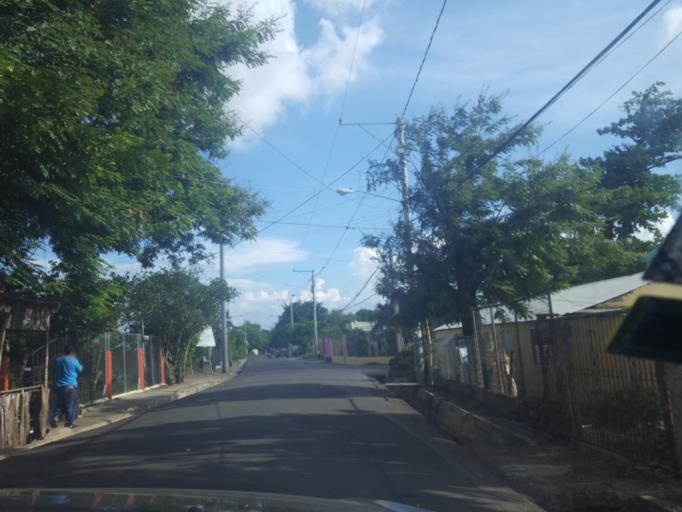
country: DO
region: Santiago
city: Licey al Medio
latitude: 19.3769
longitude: -70.6234
